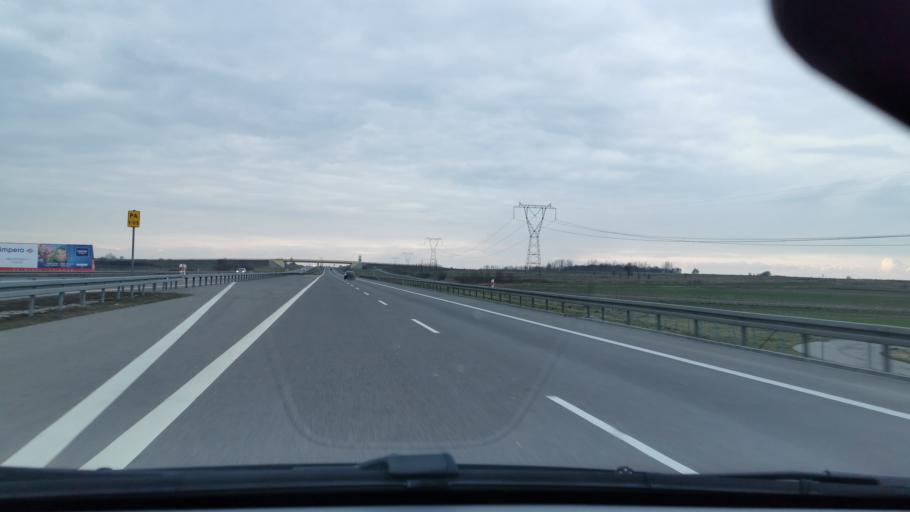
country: PL
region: Lublin Voivodeship
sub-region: Powiat pulawski
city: Markuszow
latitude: 51.3850
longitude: 22.2695
